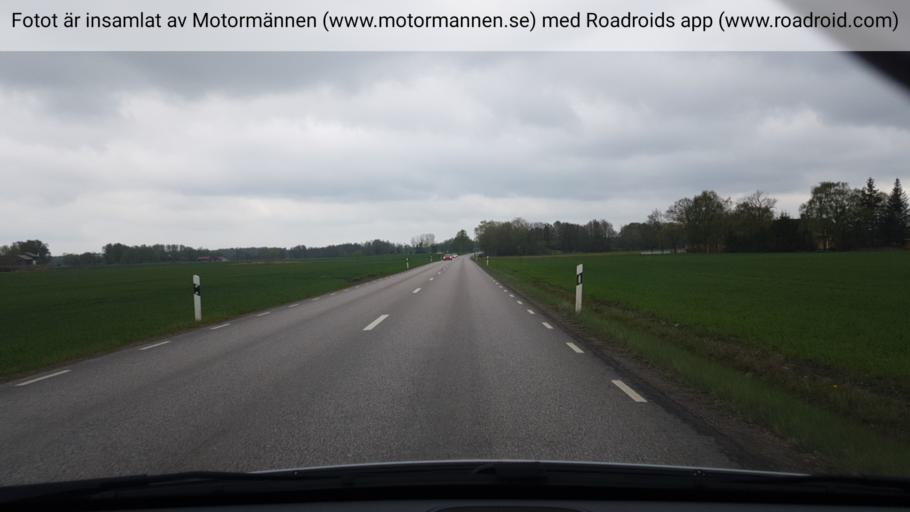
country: SE
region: Vaestra Goetaland
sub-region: Skovde Kommun
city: Stopen
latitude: 58.4952
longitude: 13.9663
